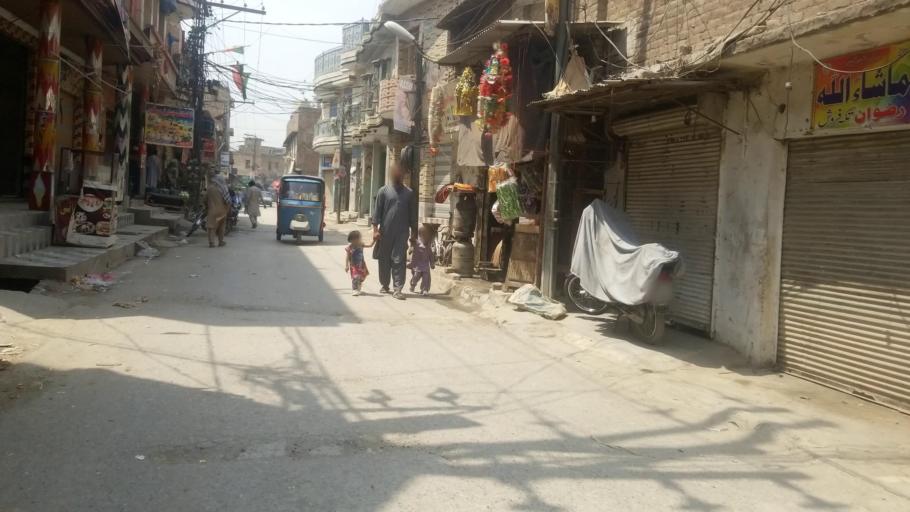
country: PK
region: Khyber Pakhtunkhwa
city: Peshawar
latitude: 34.0269
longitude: 71.5820
